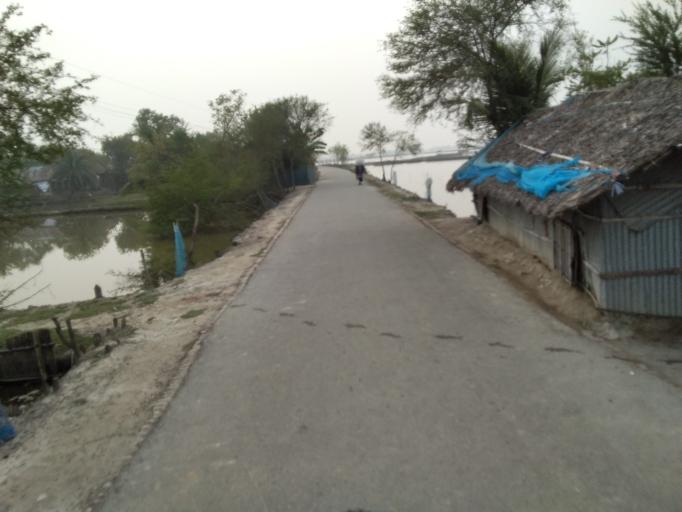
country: IN
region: West Bengal
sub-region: North 24 Parganas
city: Taki
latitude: 22.5833
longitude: 89.0579
